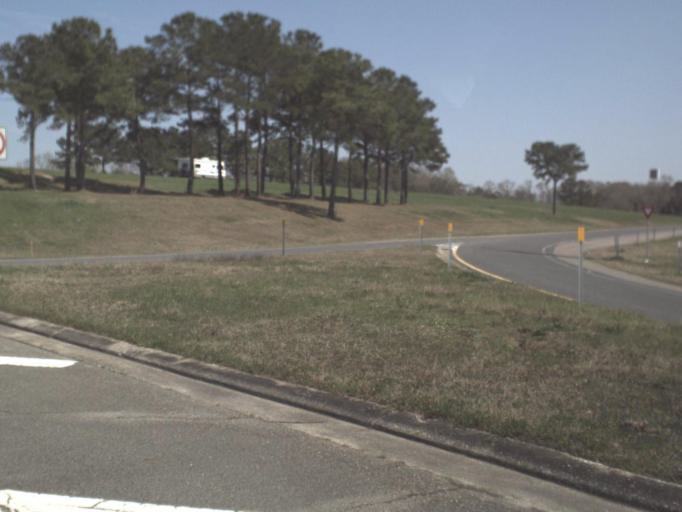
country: US
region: Florida
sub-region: Gadsden County
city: Gretna
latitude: 30.5773
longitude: -84.7006
